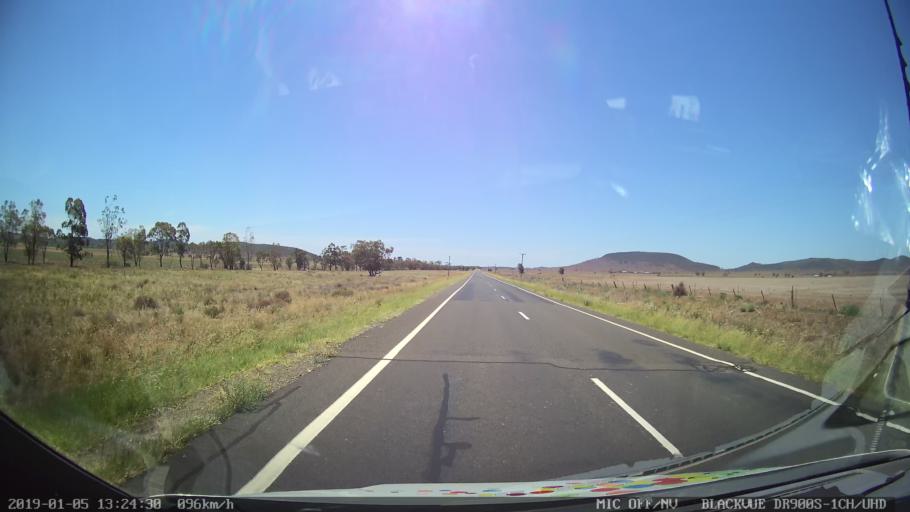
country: AU
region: New South Wales
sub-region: Gunnedah
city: Gunnedah
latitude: -31.0689
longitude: 149.9899
